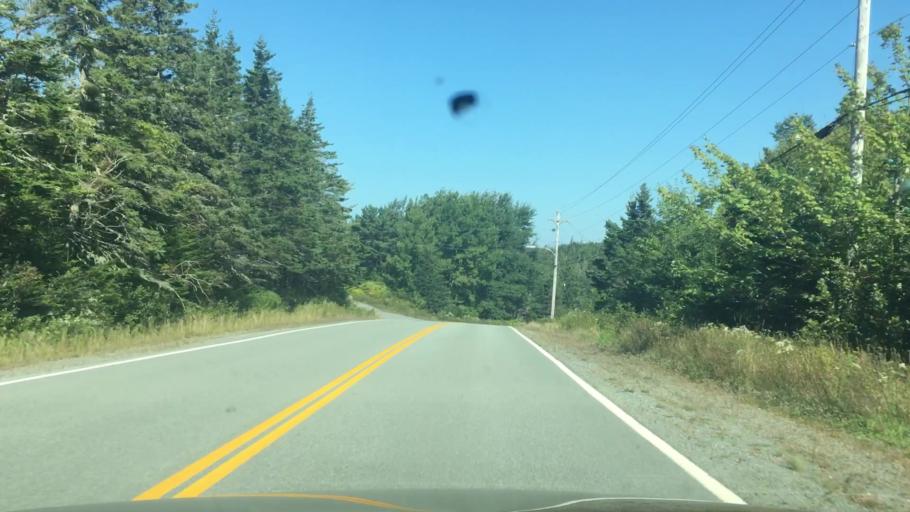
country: CA
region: Nova Scotia
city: New Glasgow
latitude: 44.8200
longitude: -62.6343
